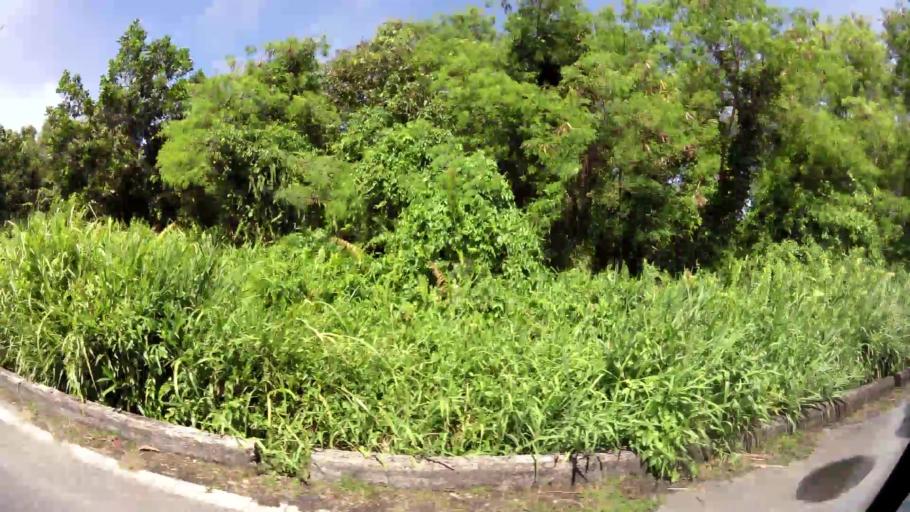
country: BN
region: Belait
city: Kuala Belait
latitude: 4.5857
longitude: 114.2190
